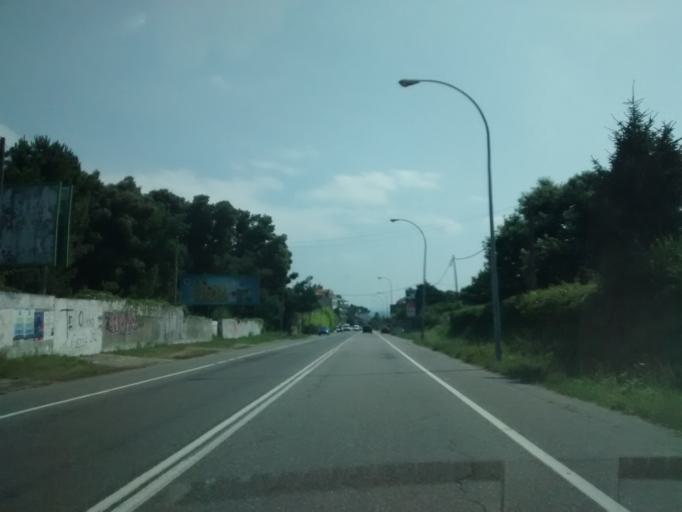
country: ES
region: Galicia
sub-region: Provincia de Pontevedra
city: Sanxenxo
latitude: 42.4049
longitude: -8.8168
